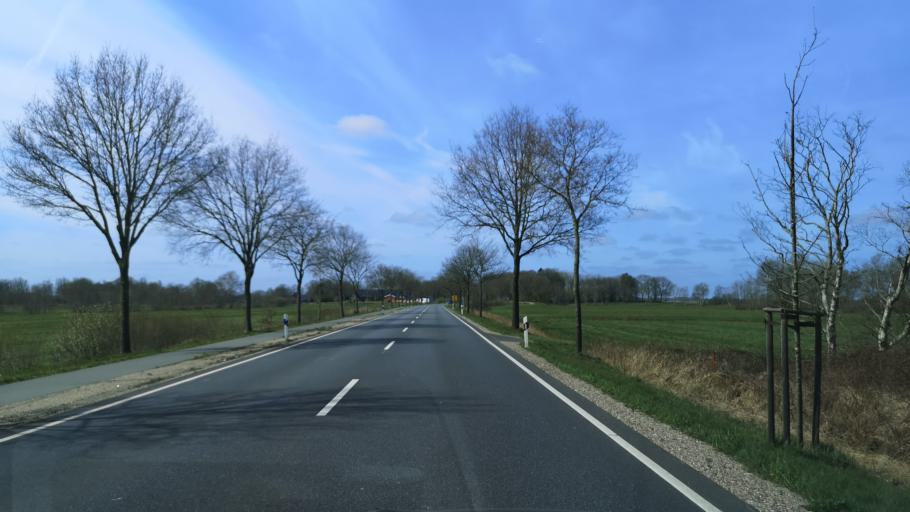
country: DE
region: Schleswig-Holstein
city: Prinzenmoor
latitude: 54.2220
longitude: 9.4626
